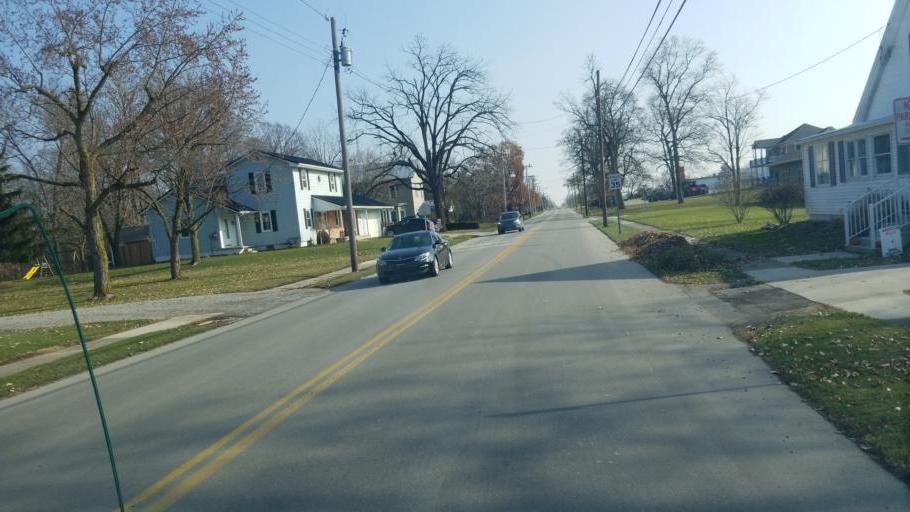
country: US
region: Ohio
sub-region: Mercer County
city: Fort Recovery
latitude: 40.4130
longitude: -84.7723
